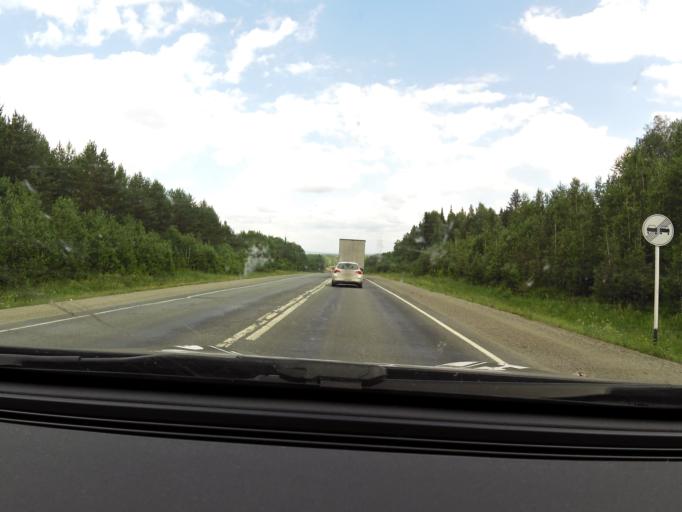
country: RU
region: Sverdlovsk
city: Bisert'
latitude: 56.8273
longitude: 59.0021
